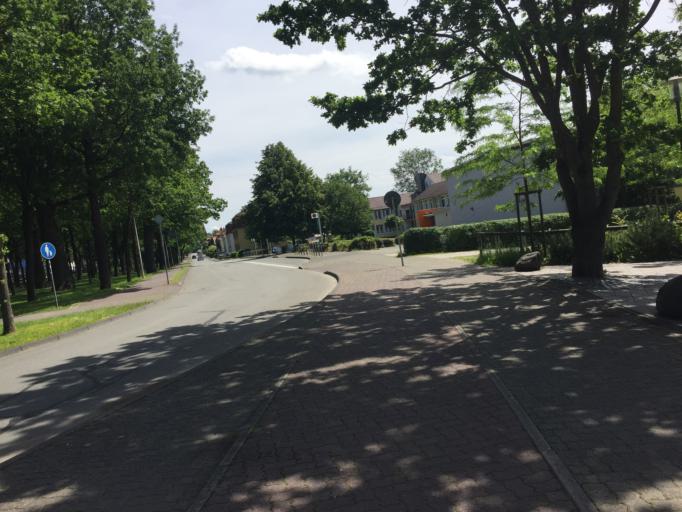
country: DE
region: Hesse
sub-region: Regierungsbezirk Kassel
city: Bad Arolsen
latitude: 51.3786
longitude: 9.0039
